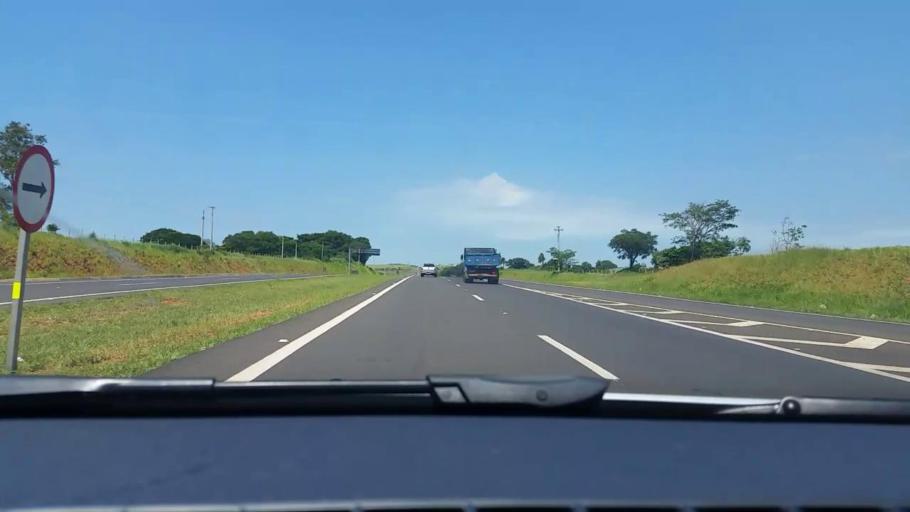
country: BR
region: Sao Paulo
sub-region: Bauru
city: Bauru
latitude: -22.3782
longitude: -49.0618
